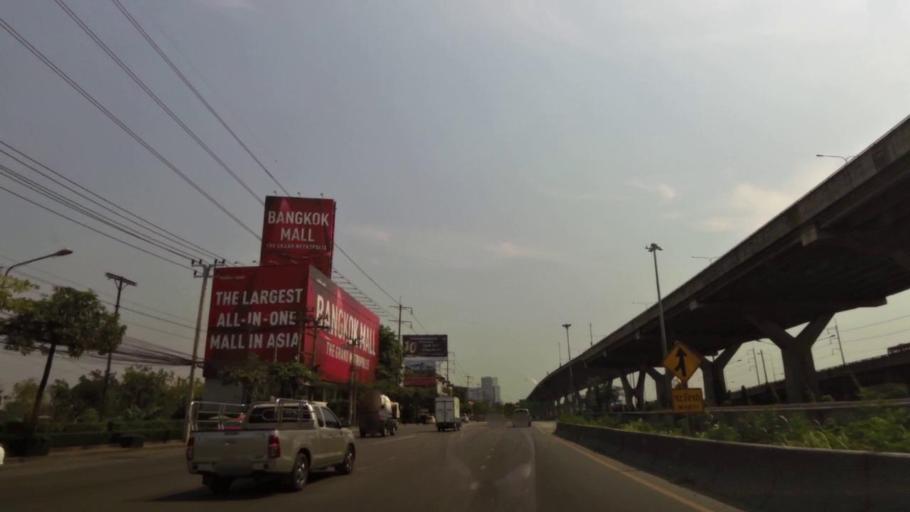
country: TH
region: Bangkok
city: Phra Khanong
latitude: 13.6728
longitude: 100.6102
